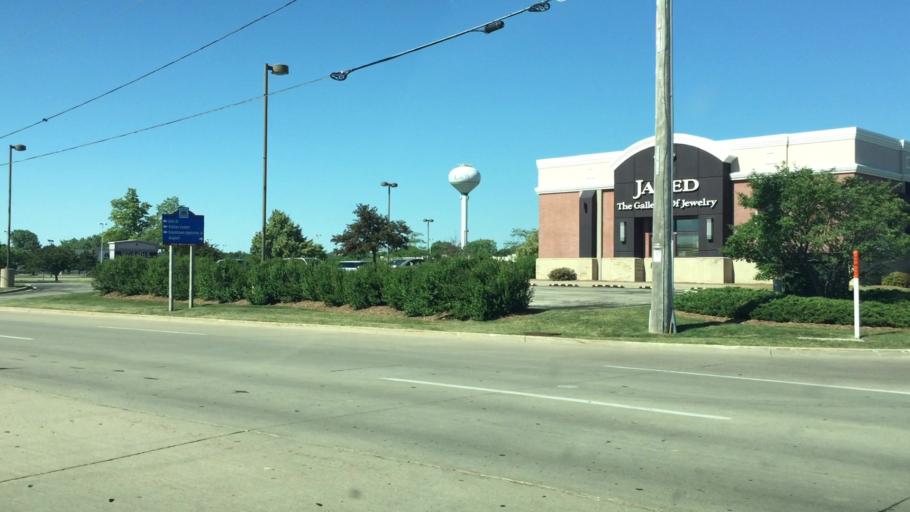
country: US
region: Wisconsin
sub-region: Outagamie County
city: Appleton
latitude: 44.2634
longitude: -88.4761
